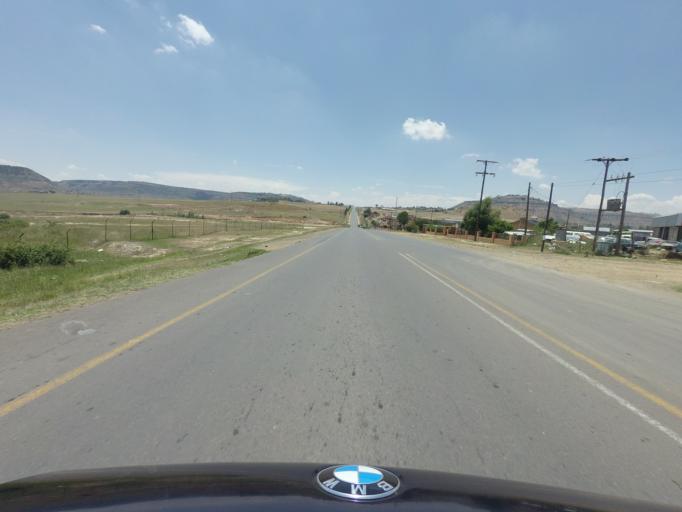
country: LS
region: Maseru
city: Maseru
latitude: -29.2652
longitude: 27.5470
